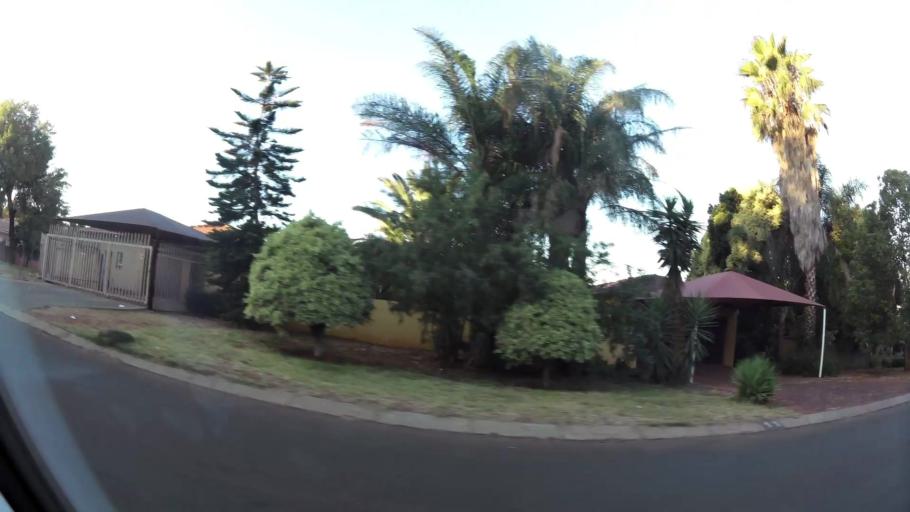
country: ZA
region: North-West
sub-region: Bojanala Platinum District Municipality
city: Rustenburg
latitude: -25.7096
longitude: 27.2331
